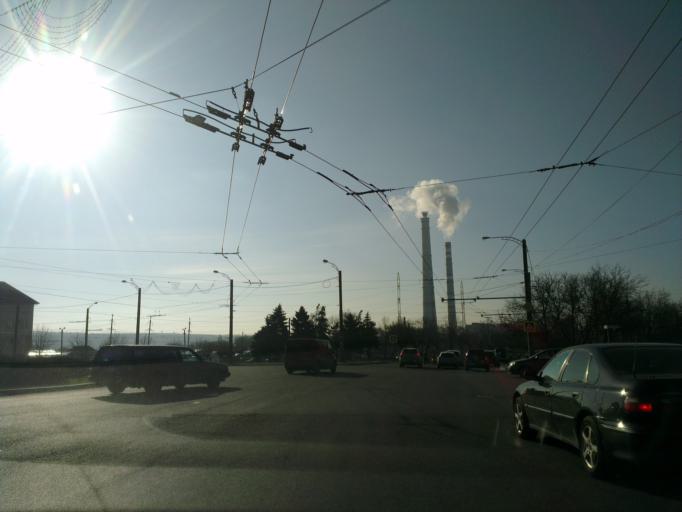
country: MD
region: Chisinau
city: Chisinau
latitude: 47.0362
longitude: 28.8887
